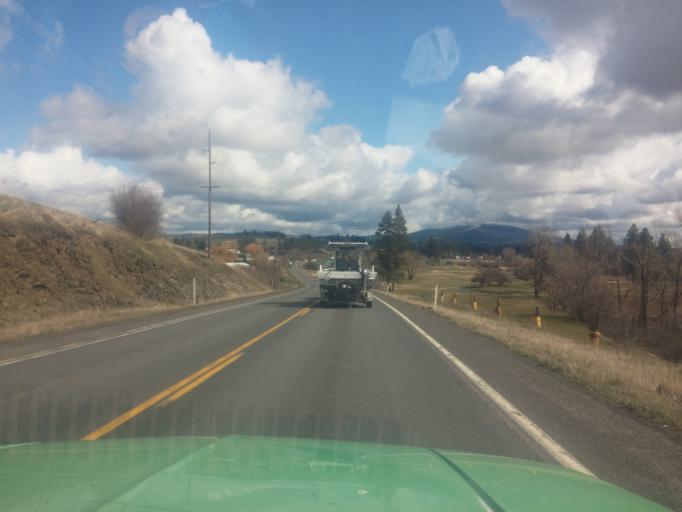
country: US
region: Idaho
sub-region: Latah County
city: Moscow
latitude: 46.9231
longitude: -116.9444
